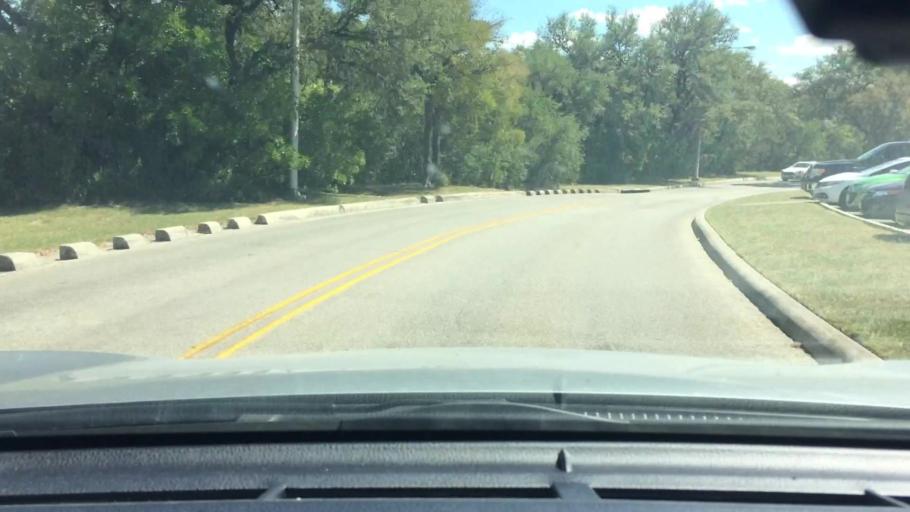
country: US
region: Texas
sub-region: Bexar County
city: Shavano Park
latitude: 29.5814
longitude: -98.6142
